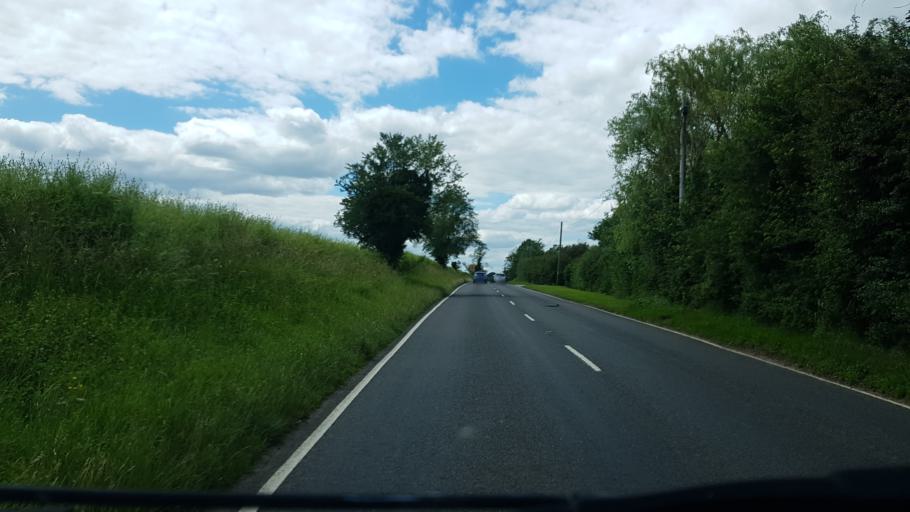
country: GB
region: England
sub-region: Worcestershire
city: Droitwich
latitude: 52.2616
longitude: -2.0886
